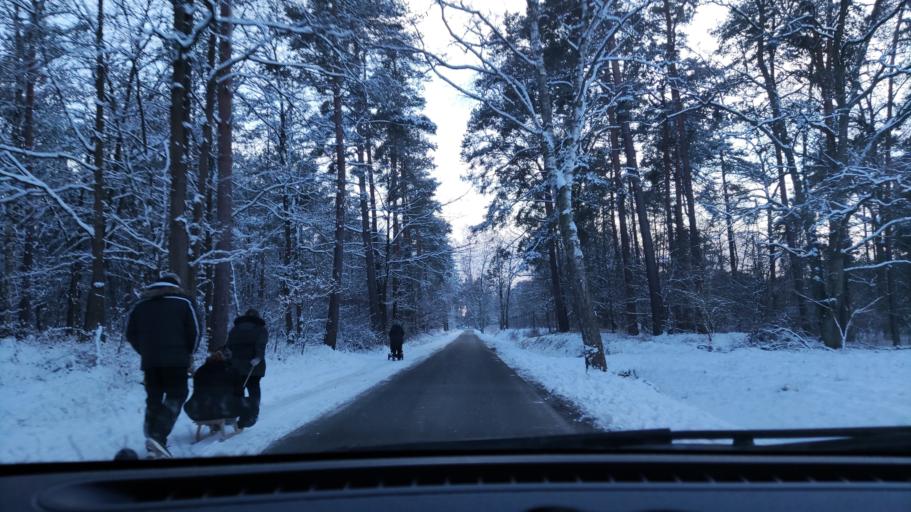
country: DE
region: Lower Saxony
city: Tosterglope
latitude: 53.2685
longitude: 10.7959
